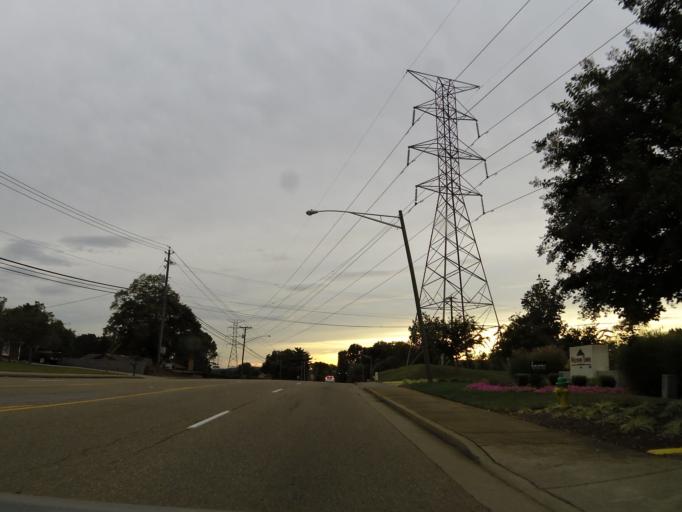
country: US
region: Tennessee
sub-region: Blount County
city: Louisville
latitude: 35.9216
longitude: -84.0395
